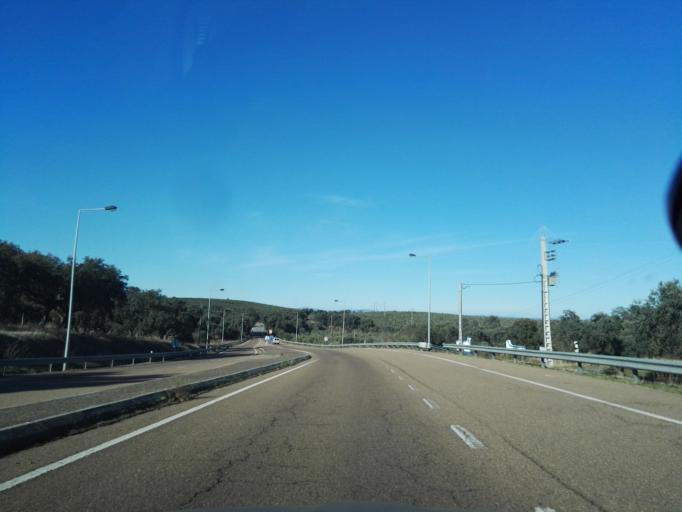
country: PT
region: Portalegre
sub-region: Elvas
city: Elvas
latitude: 38.9100
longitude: -7.1802
